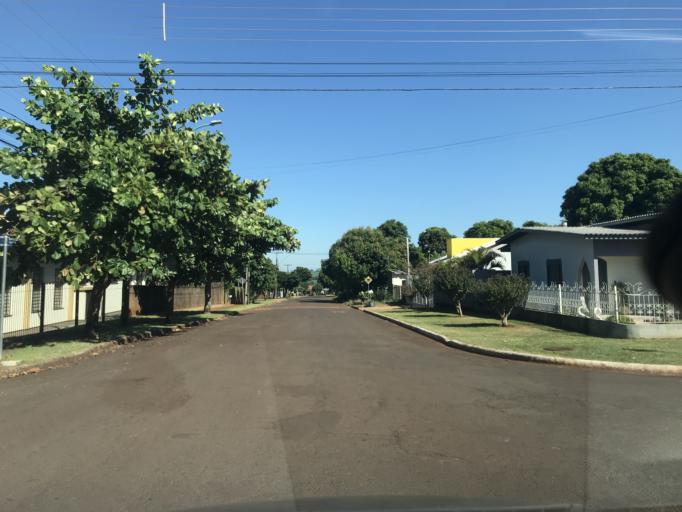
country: BR
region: Parana
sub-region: Palotina
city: Palotina
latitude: -24.2742
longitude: -53.8428
